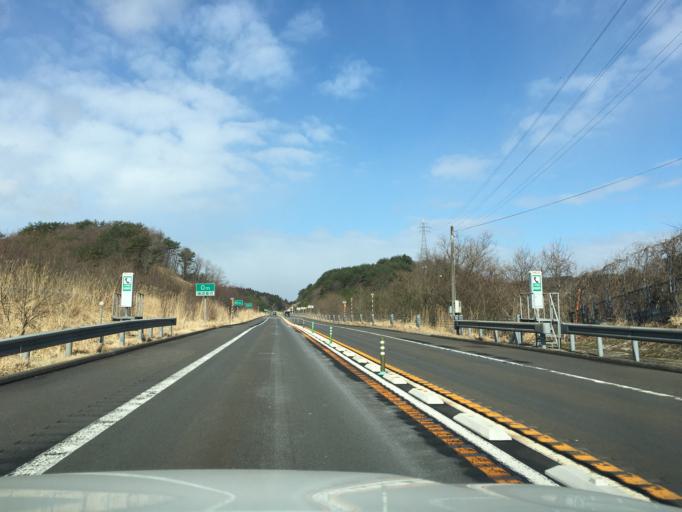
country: JP
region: Akita
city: Akita
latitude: 39.7591
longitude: 140.1326
